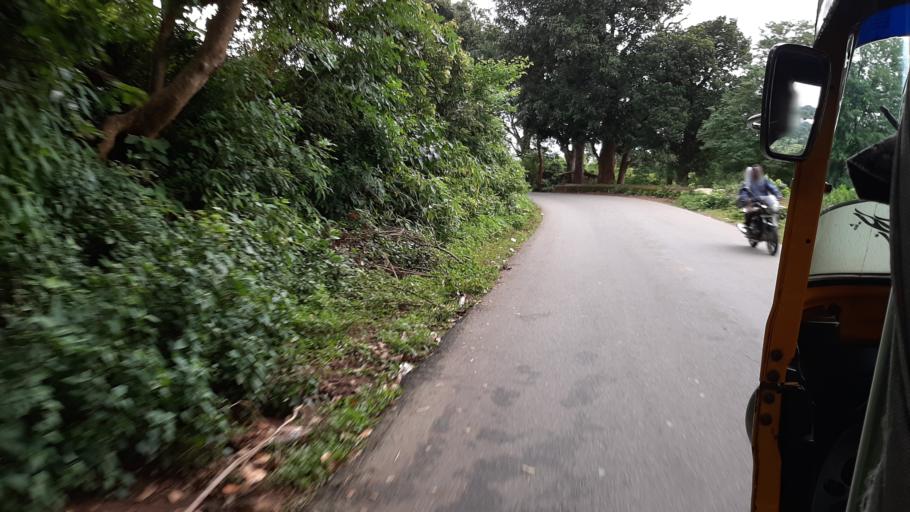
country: IN
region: Andhra Pradesh
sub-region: Vizianagaram District
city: Salur
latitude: 18.2456
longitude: 83.0252
